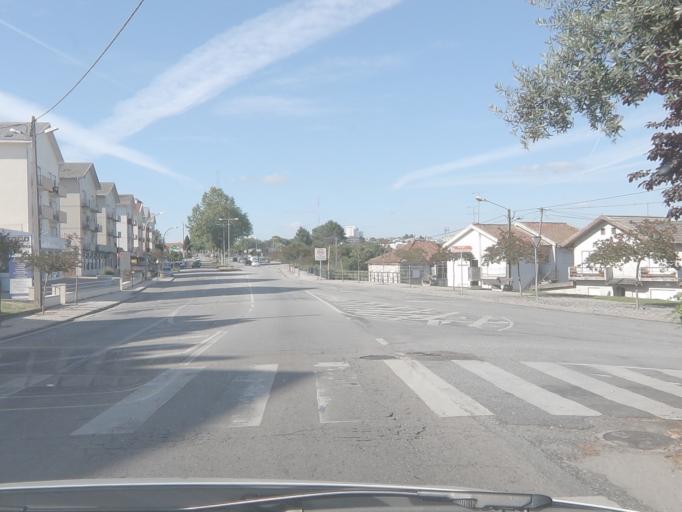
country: PT
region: Viseu
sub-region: Viseu
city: Viseu
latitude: 40.6407
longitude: -7.9251
